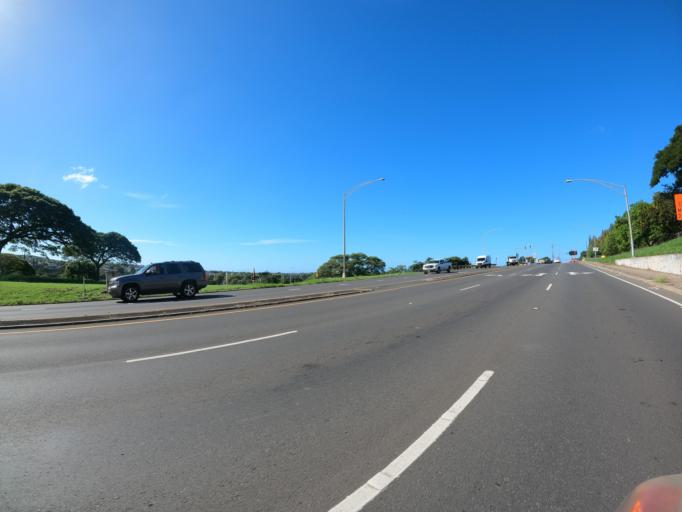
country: US
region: Hawaii
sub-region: Honolulu County
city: Halawa Heights
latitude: 21.3733
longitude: -157.9185
